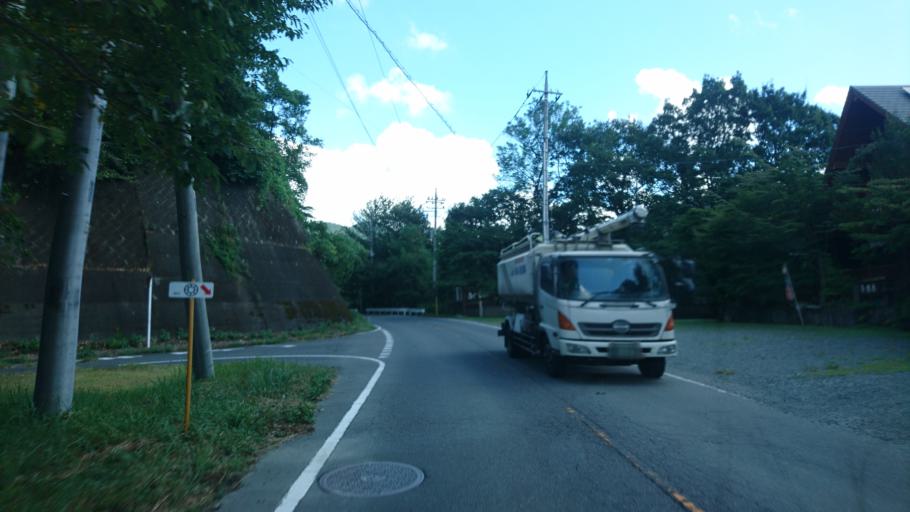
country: JP
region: Gunma
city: Omamacho-omama
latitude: 36.5239
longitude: 139.2534
